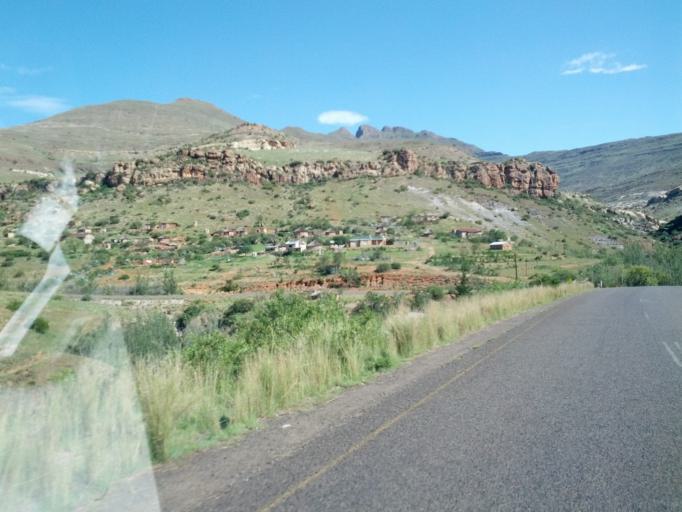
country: LS
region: Qacha's Nek
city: Qacha's Nek
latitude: -30.0723
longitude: 28.5604
